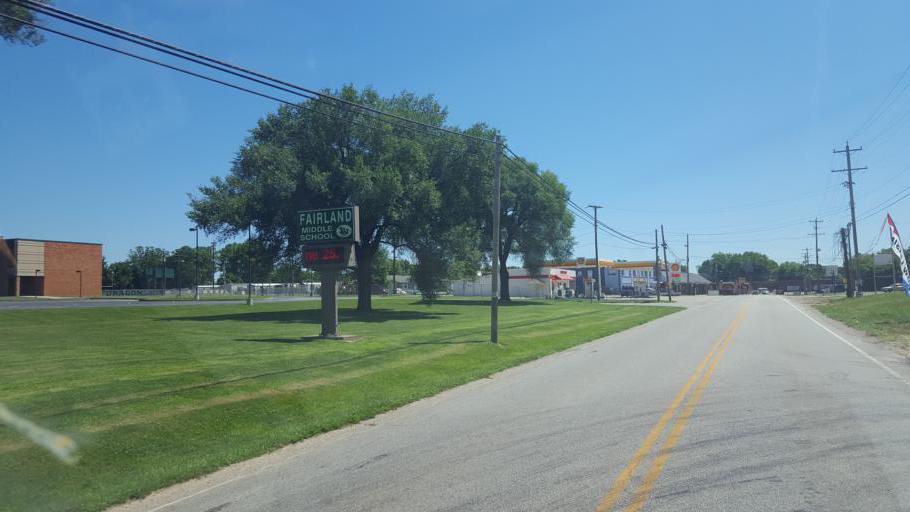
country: US
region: West Virginia
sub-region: Cabell County
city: Pea Ridge
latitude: 38.4424
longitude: -82.3582
